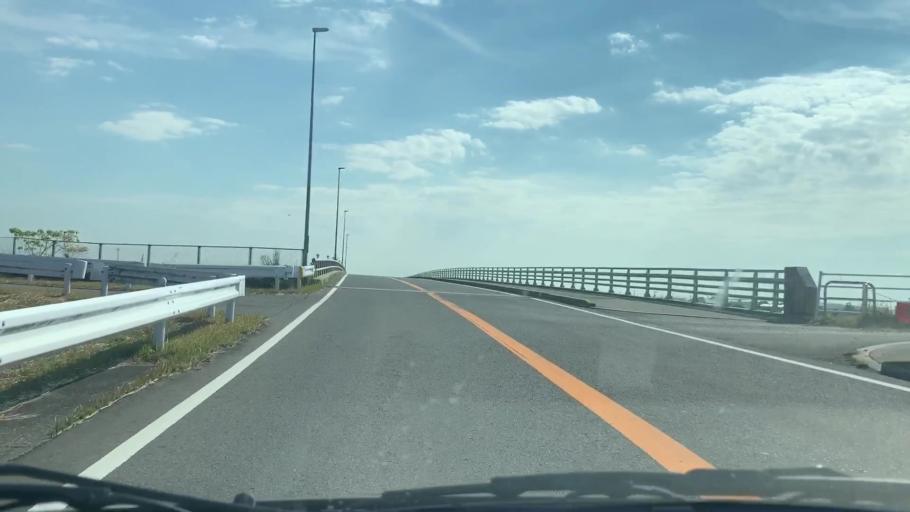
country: JP
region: Saga Prefecture
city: Saga-shi
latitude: 33.2225
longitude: 130.1928
